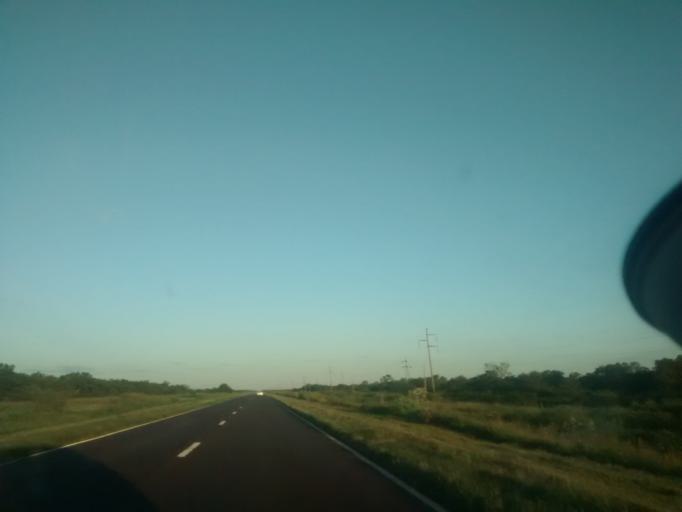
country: AR
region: Chaco
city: La Escondida
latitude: -27.0894
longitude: -59.6372
